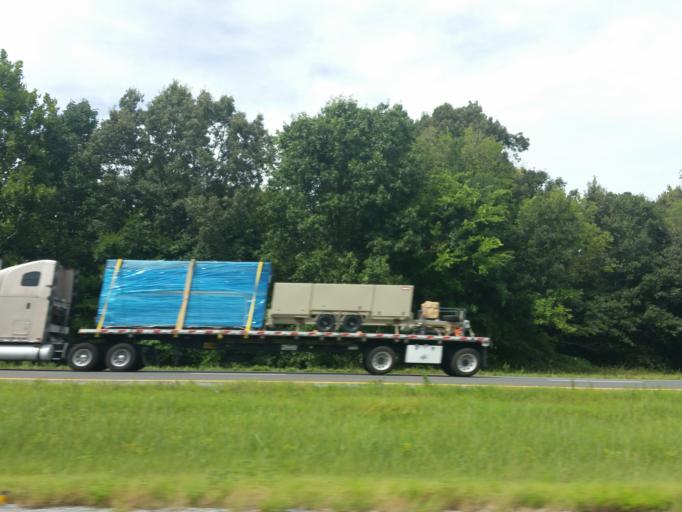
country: US
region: Kentucky
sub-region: Marshall County
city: Calvert City
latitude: 36.9918
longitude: -88.4127
